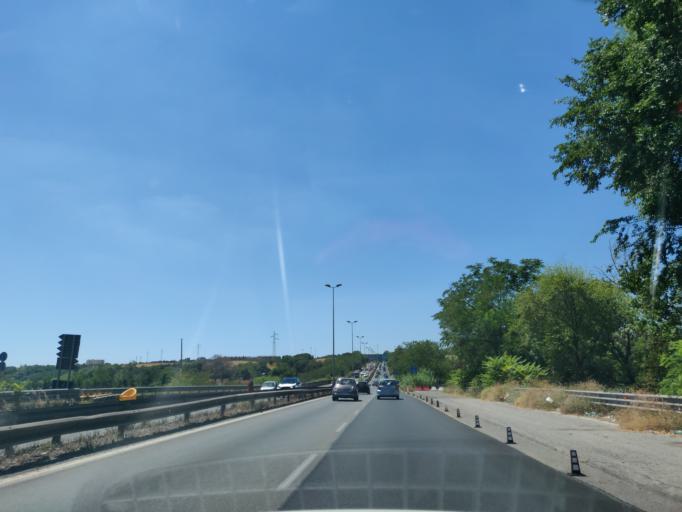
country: IT
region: Latium
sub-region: Citta metropolitana di Roma Capitale
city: Selcetta
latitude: 41.8099
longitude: 12.4580
